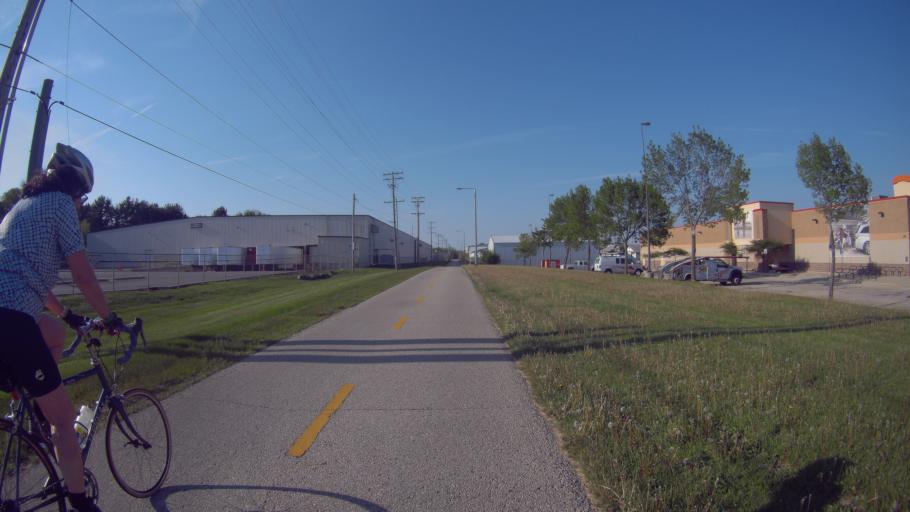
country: US
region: Wisconsin
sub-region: Dane County
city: Shorewood Hills
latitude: 43.0346
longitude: -89.4594
